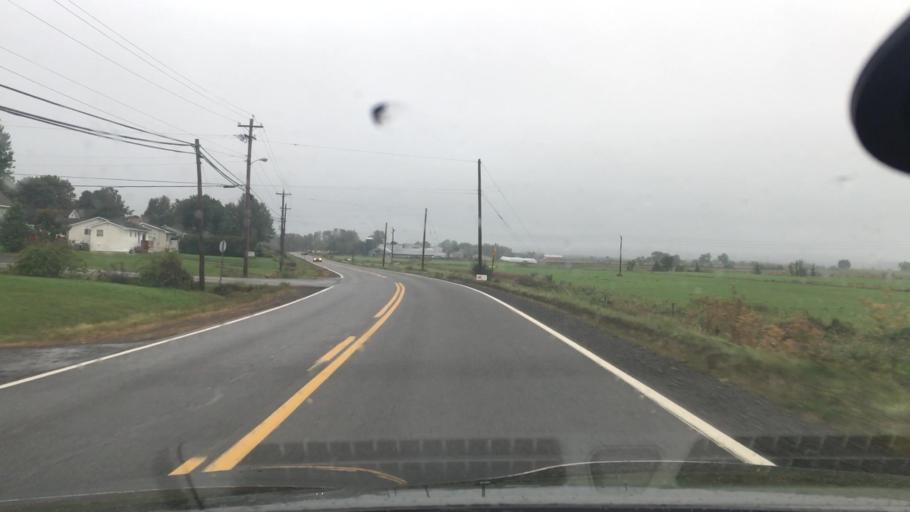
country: CA
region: Nova Scotia
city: Windsor
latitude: 44.9748
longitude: -64.1363
